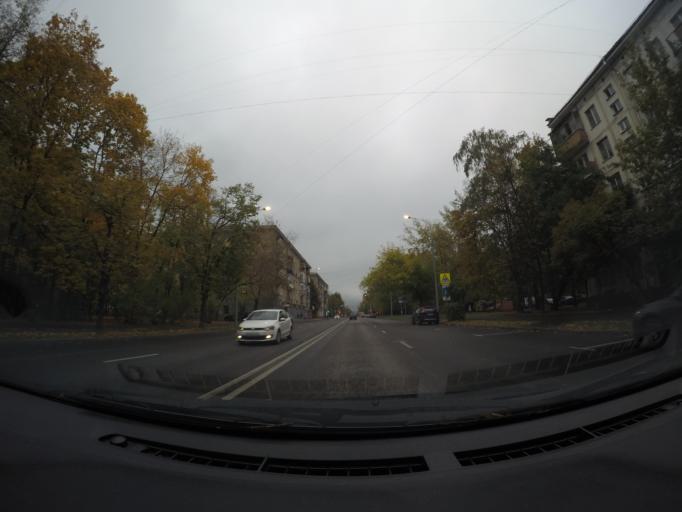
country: RU
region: Moskovskaya
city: Novogireyevo
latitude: 55.7570
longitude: 37.7993
